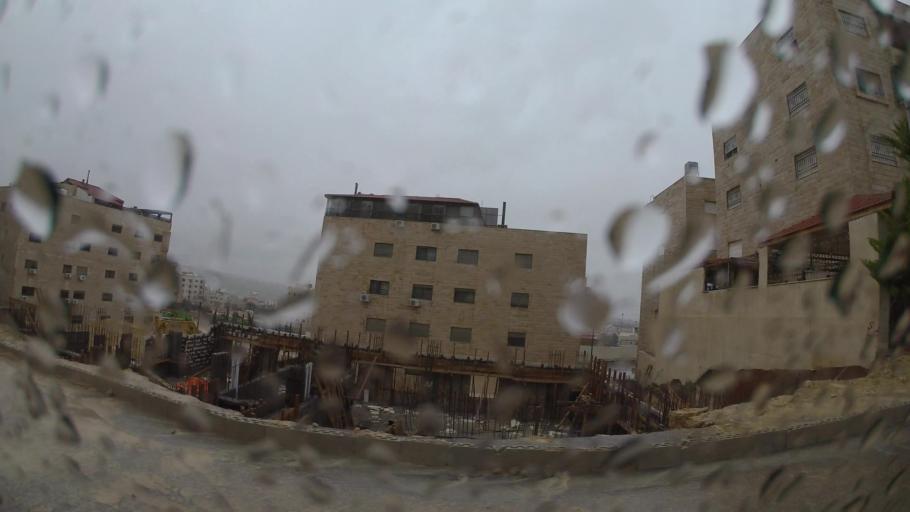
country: JO
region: Amman
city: Al Jubayhah
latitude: 32.0267
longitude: 35.8899
